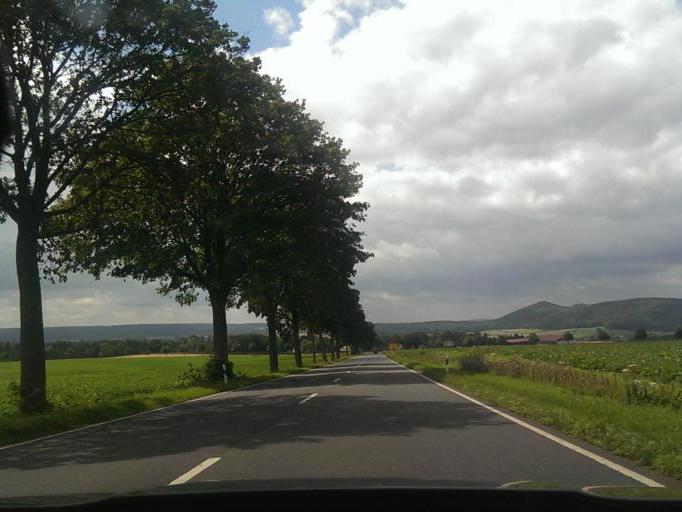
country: DE
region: Lower Saxony
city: Holenberg
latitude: 51.9031
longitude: 9.6017
